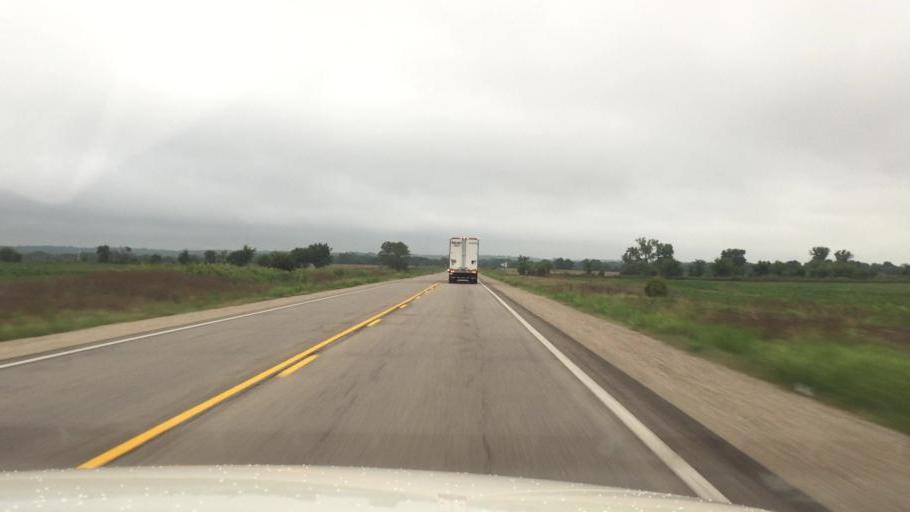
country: US
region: Kansas
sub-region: Montgomery County
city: Cherryvale
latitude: 37.1973
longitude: -95.5825
